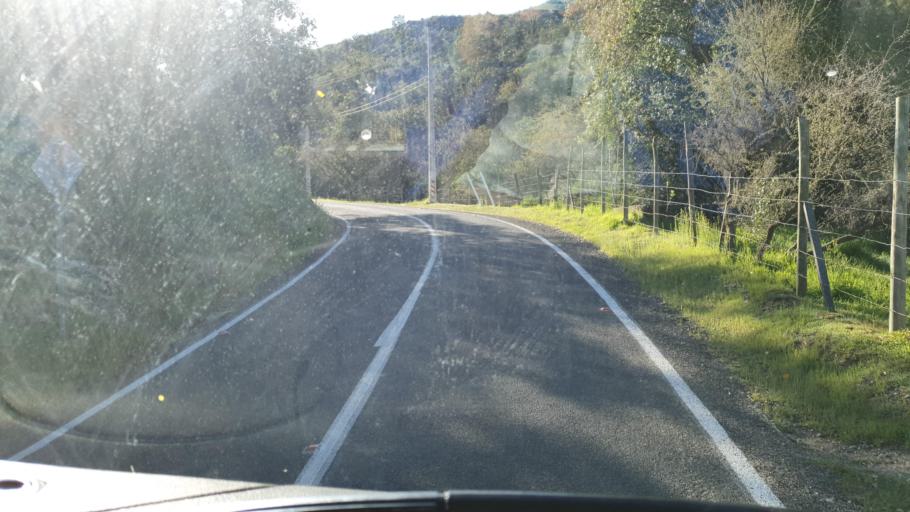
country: CL
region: Valparaiso
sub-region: Provincia de Marga Marga
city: Limache
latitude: -33.1792
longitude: -71.1822
